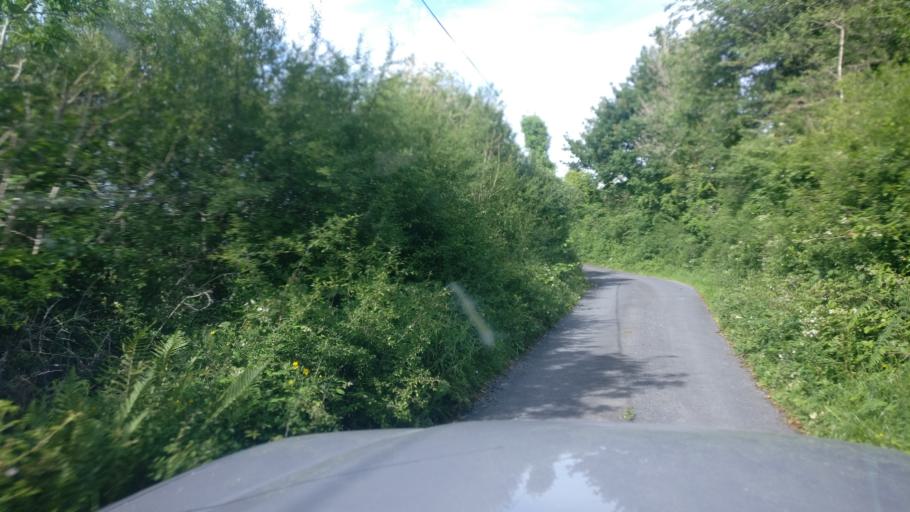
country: IE
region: Connaught
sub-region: County Galway
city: Gort
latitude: 53.0957
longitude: -8.6981
